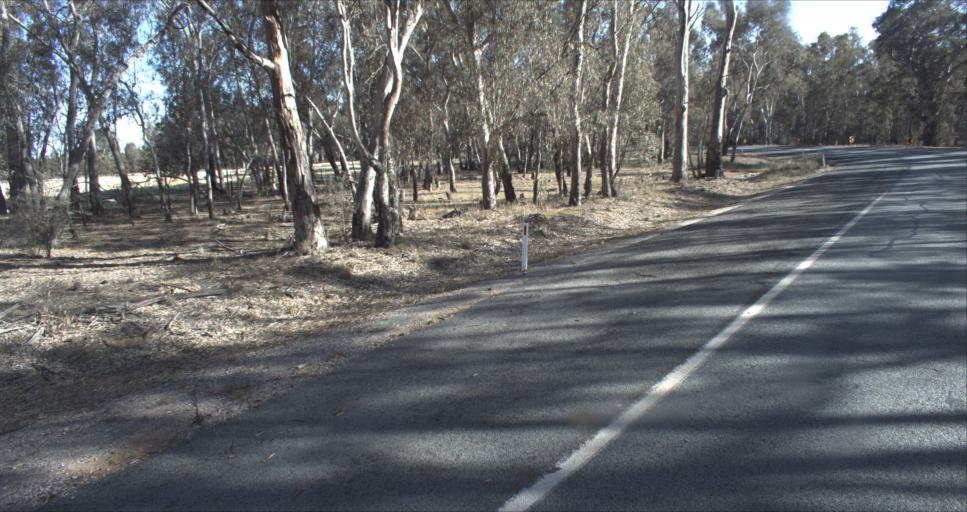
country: AU
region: New South Wales
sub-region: Leeton
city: Leeton
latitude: -34.6311
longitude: 146.3753
